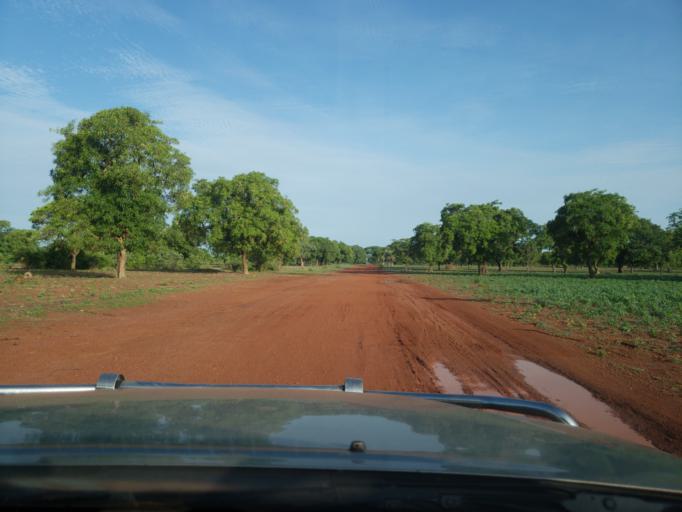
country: ML
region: Sikasso
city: Koutiala
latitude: 12.4245
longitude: -5.5927
